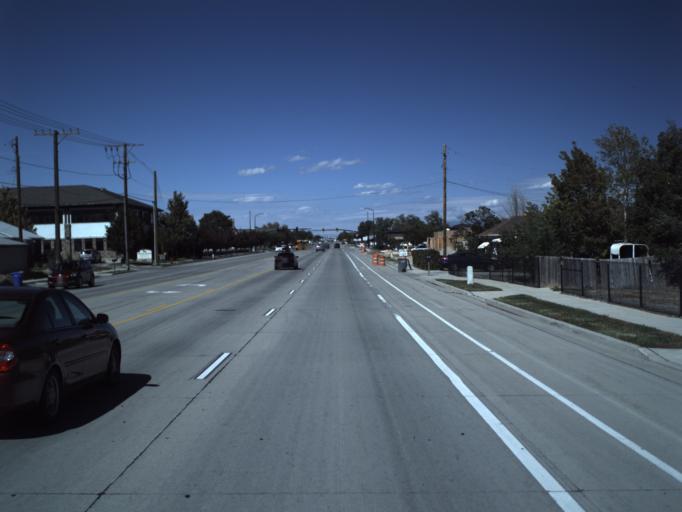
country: US
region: Utah
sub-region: Salt Lake County
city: South Jordan
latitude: 40.5486
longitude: -111.9386
